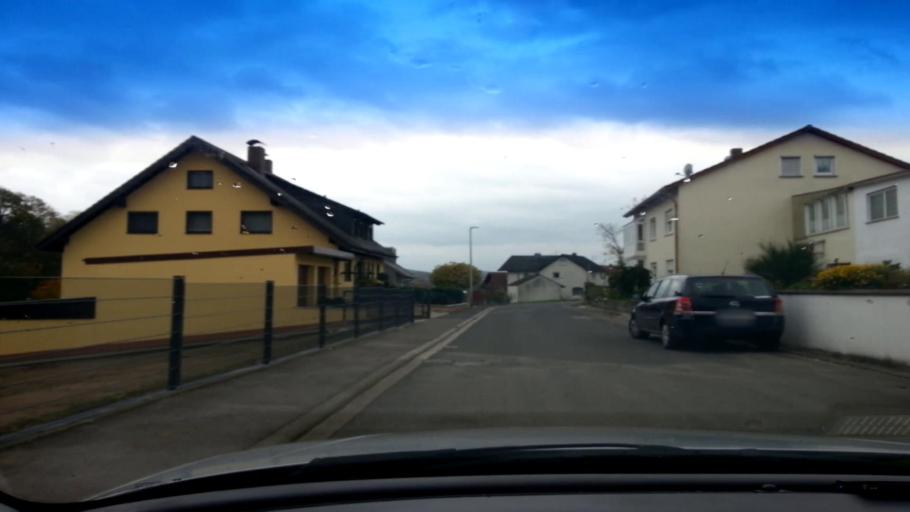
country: DE
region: Bavaria
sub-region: Regierungsbezirk Unterfranken
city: Stettfeld
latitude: 49.9744
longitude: 10.7296
